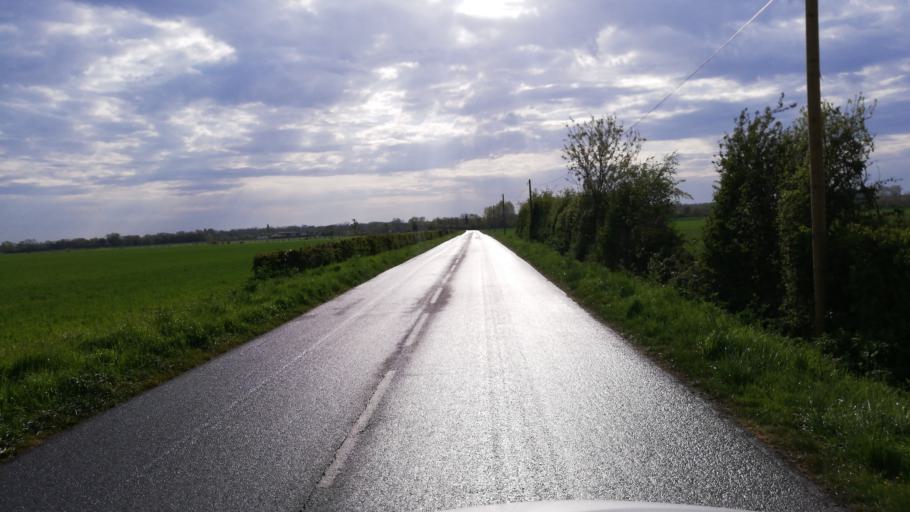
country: FR
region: Pays de la Loire
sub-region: Departement de la Vendee
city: Maillezais
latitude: 46.3250
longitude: -0.7282
